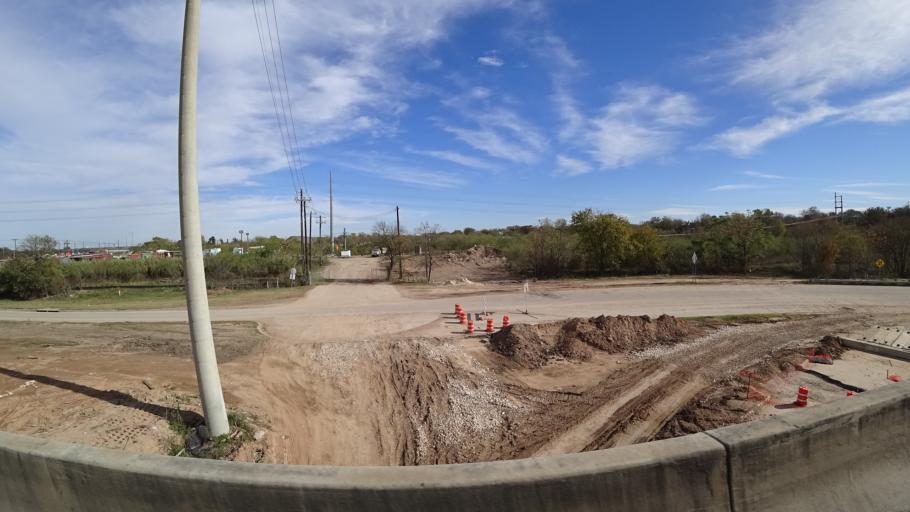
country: US
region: Texas
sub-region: Travis County
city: Austin
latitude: 30.2478
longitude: -97.6903
